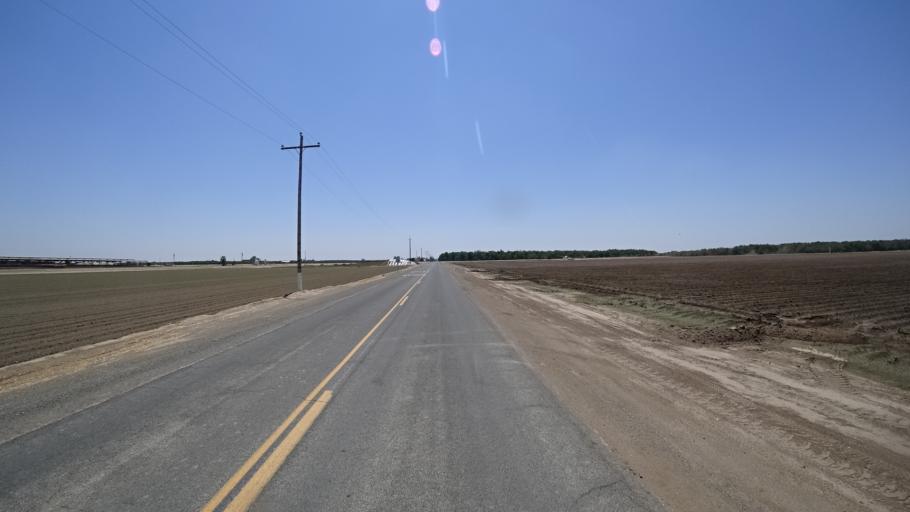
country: US
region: California
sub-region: Kings County
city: Armona
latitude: 36.3417
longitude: -119.7270
